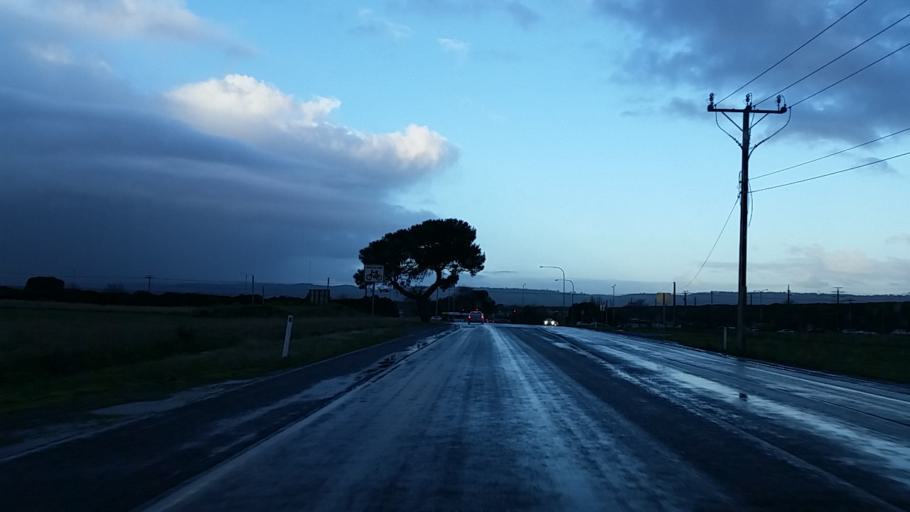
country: AU
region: South Australia
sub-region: Onkaparinga
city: Bedford Park
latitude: -35.0538
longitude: 138.5571
